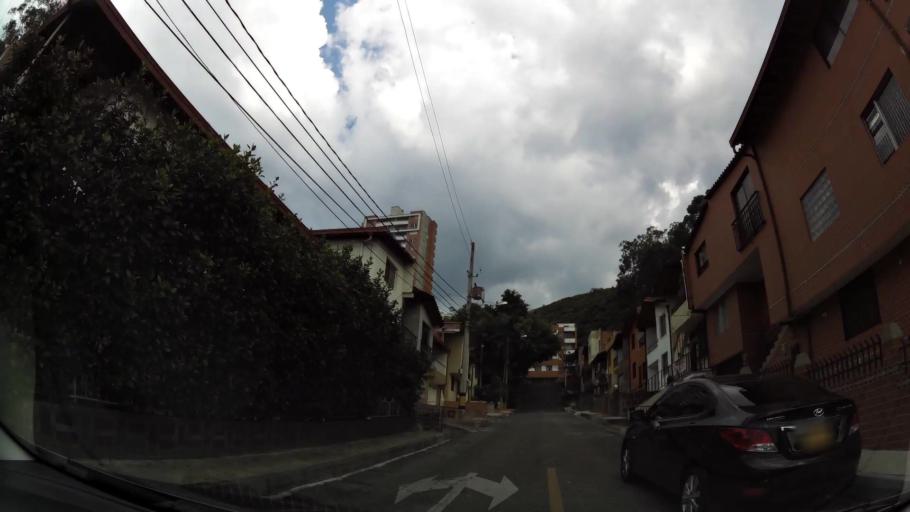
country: CO
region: Antioquia
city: Envigado
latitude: 6.1577
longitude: -75.5937
